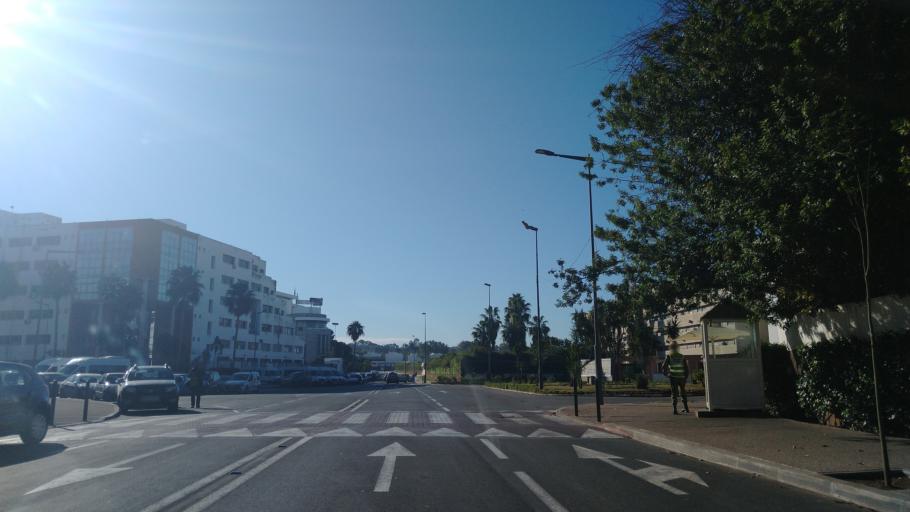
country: MA
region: Rabat-Sale-Zemmour-Zaer
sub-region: Rabat
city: Rabat
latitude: 33.9956
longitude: -6.8595
